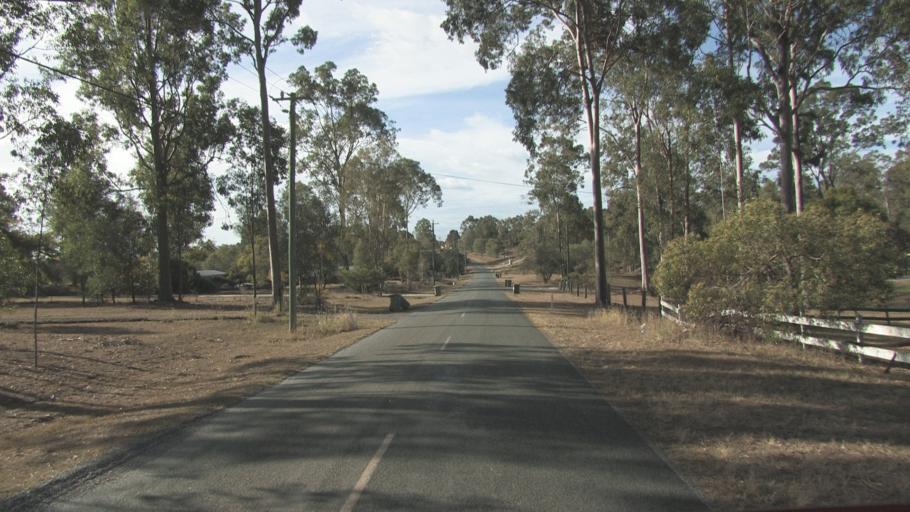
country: AU
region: Queensland
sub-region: Logan
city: Cedar Vale
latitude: -27.8787
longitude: 153.0009
